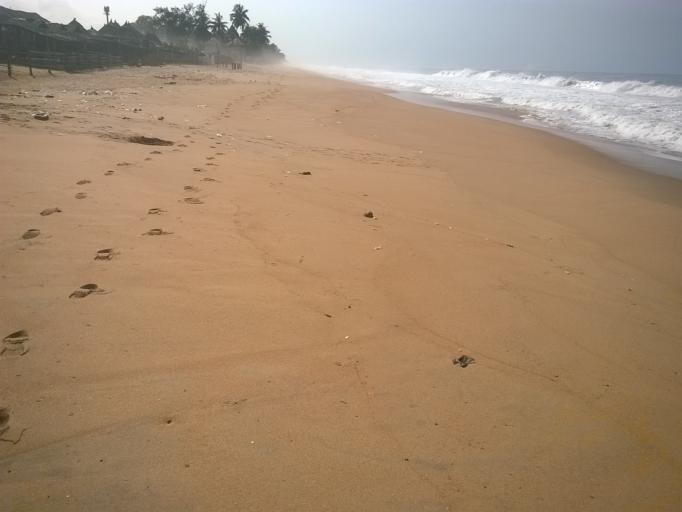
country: CI
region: Sud-Comoe
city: Grand-Bassam
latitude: 5.1967
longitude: -3.7507
